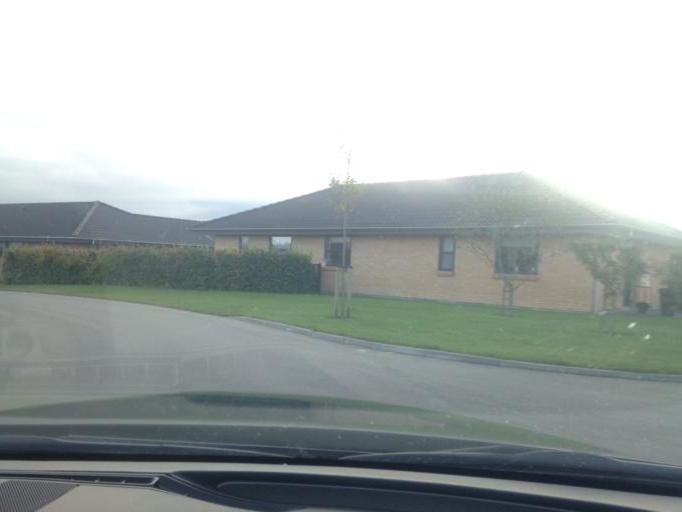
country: DK
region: South Denmark
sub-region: Kolding Kommune
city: Kolding
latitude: 55.5640
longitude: 9.4785
